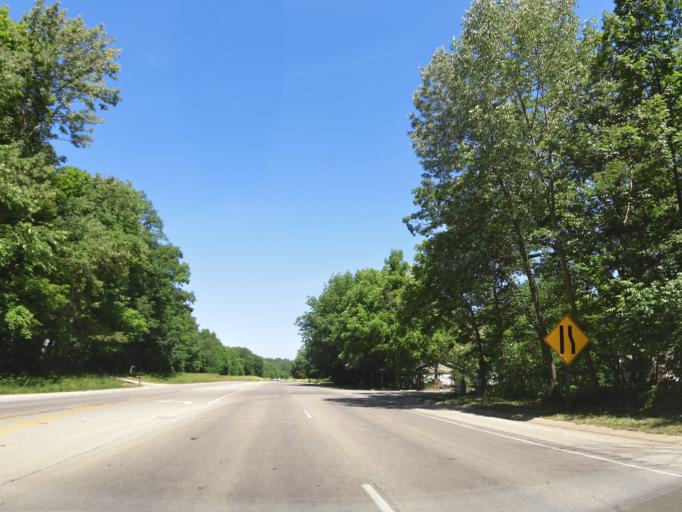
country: US
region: Illinois
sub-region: Vermilion County
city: Danville
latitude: 40.2073
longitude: -87.6340
